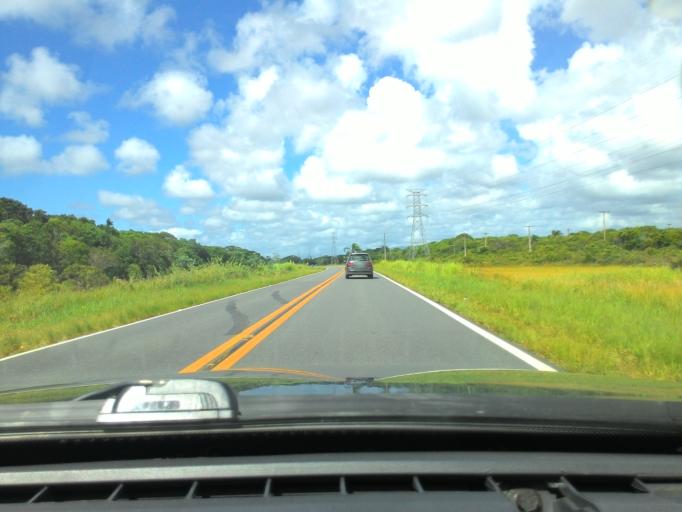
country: BR
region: Sao Paulo
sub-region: Iguape
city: Iguape
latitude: -24.7537
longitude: -47.6269
